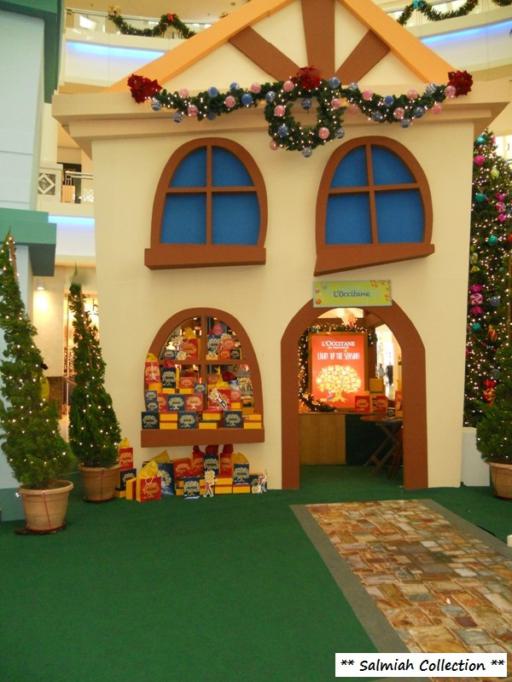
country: MY
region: Selangor
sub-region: Petaling
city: Petaling Jaya
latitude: 3.1572
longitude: 101.6097
